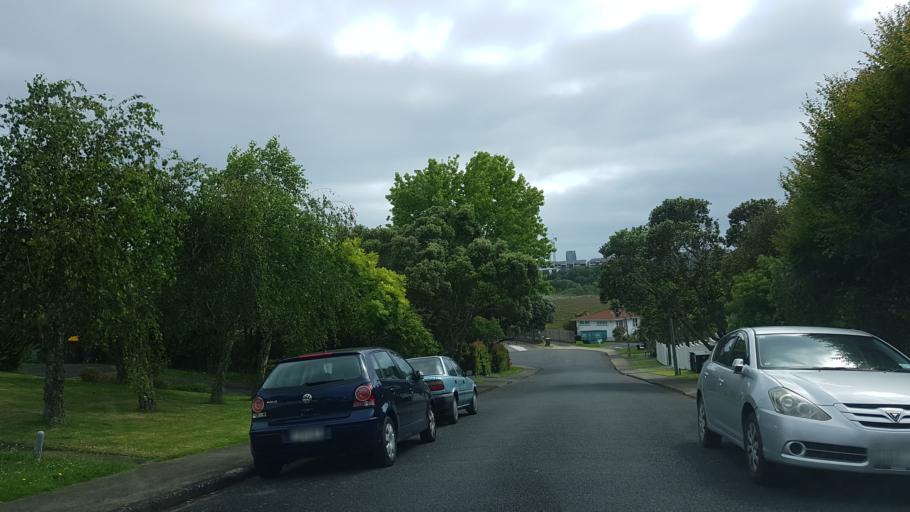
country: NZ
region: Auckland
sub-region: Auckland
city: North Shore
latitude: -36.8028
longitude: 174.7491
